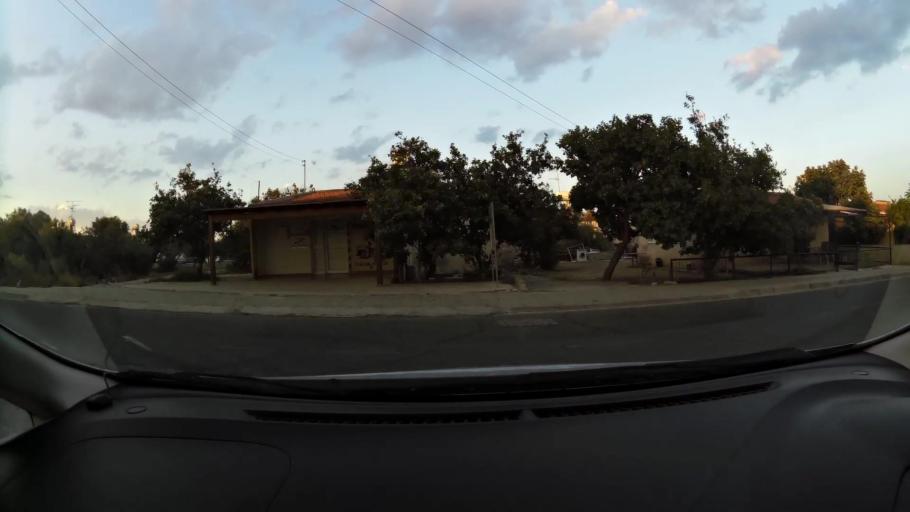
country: CY
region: Larnaka
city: Dhromolaxia
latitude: 34.8707
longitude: 33.5857
